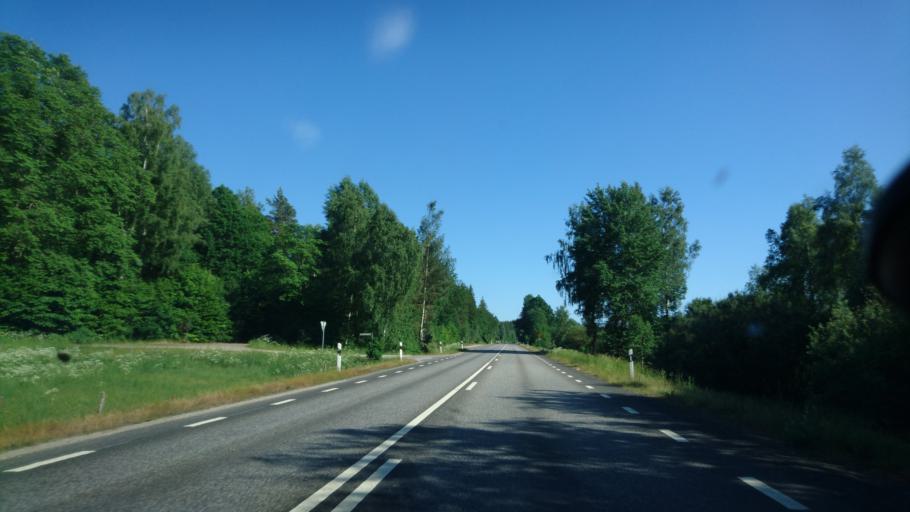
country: SE
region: Blekinge
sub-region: Olofstroms Kommun
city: Olofstroem
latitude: 56.3438
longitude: 14.4896
